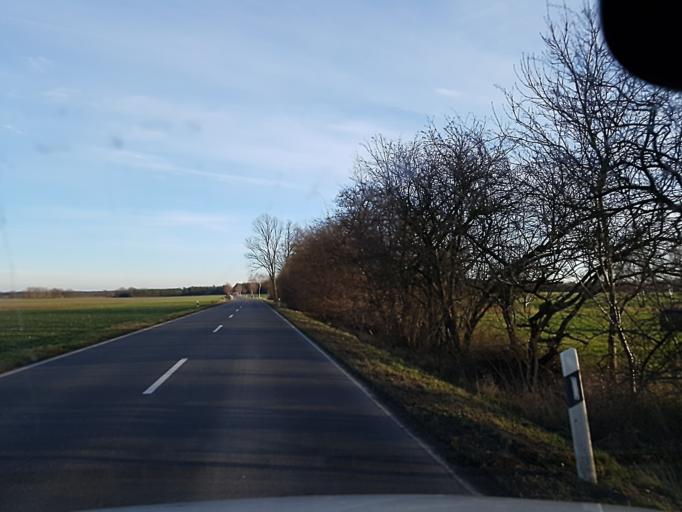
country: DE
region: Brandenburg
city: Finsterwalde
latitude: 51.6210
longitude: 13.7325
